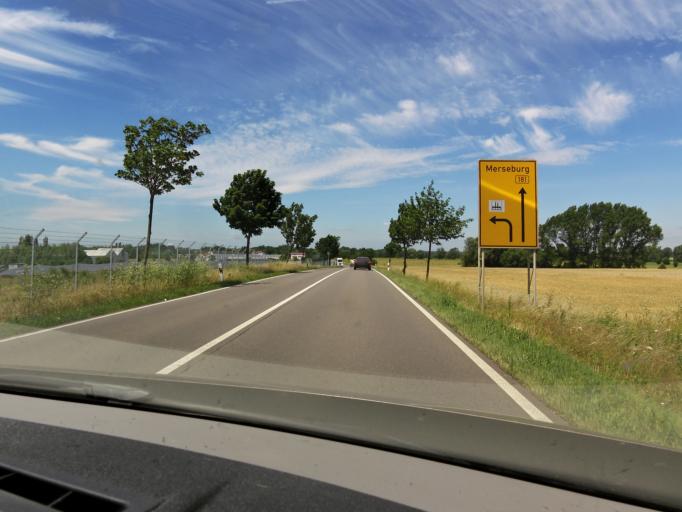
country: DE
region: Saxony-Anhalt
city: Zoschen
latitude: 51.3532
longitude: 12.1348
